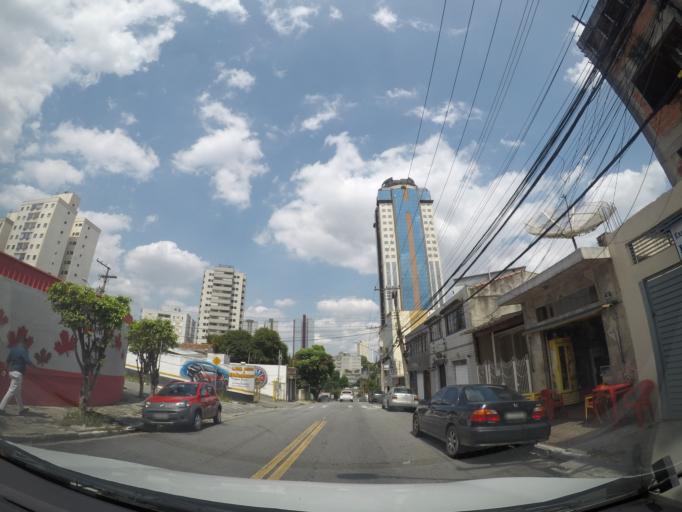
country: BR
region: Sao Paulo
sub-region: Guarulhos
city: Guarulhos
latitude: -23.4701
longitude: -46.5365
